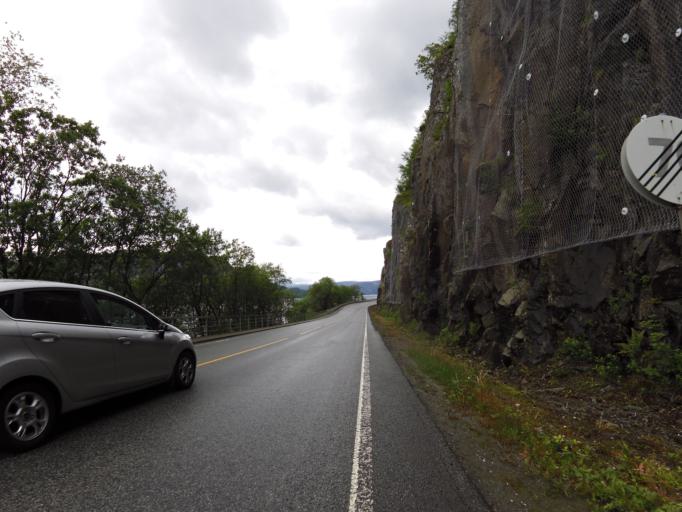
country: NO
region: Vest-Agder
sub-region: Farsund
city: Farsund
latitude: 58.0972
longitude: 6.8155
